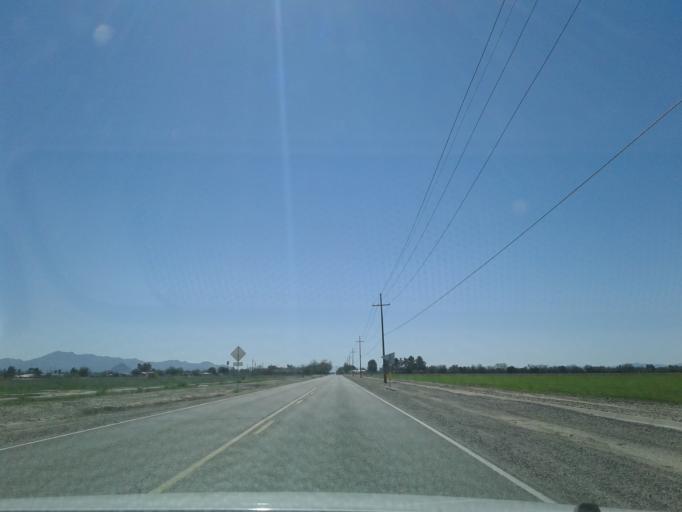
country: US
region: Arizona
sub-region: Pima County
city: Marana
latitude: 32.4453
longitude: -111.2341
